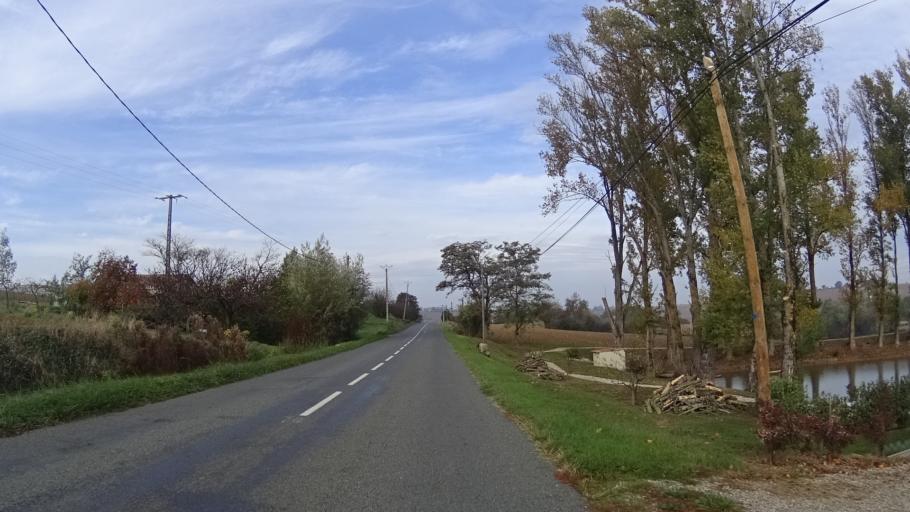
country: FR
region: Aquitaine
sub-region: Departement du Lot-et-Garonne
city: Laplume
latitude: 44.1001
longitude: 0.5583
